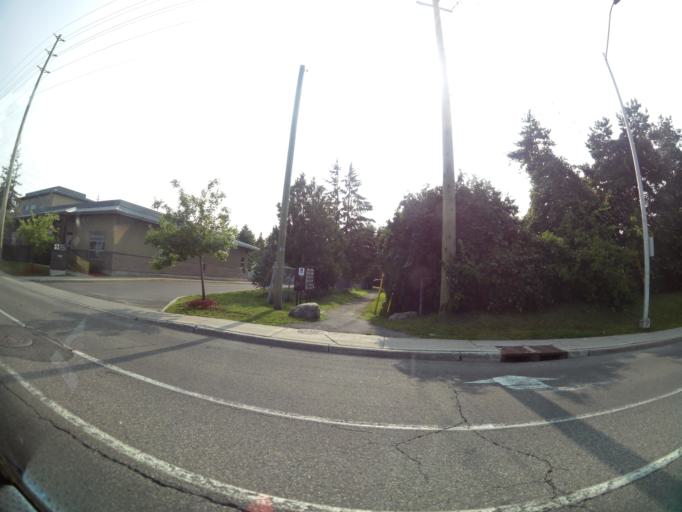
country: CA
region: Quebec
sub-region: Outaouais
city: Gatineau
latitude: 45.4616
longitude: -75.4883
